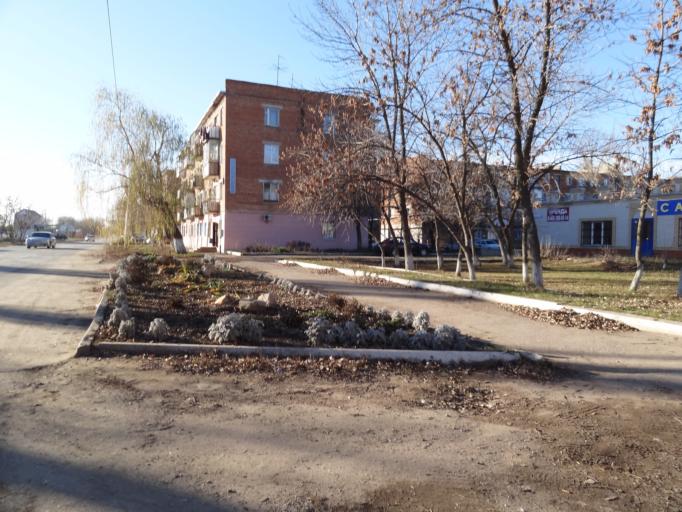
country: RU
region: Saratov
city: Engel's
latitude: 51.4693
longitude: 46.1497
